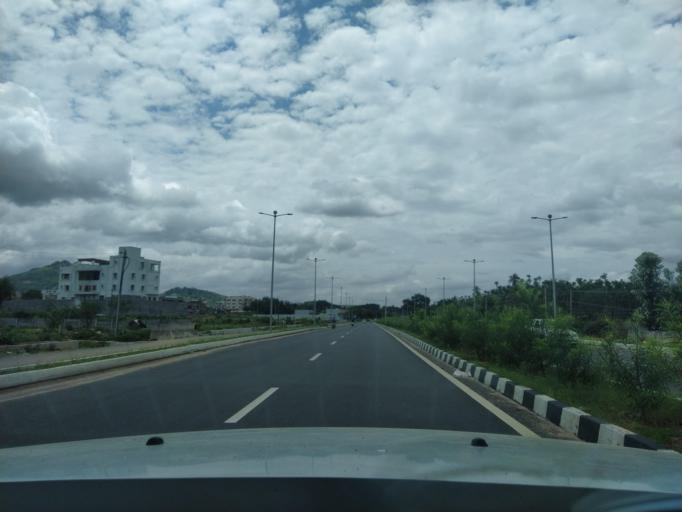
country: IN
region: Karnataka
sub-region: Tumkur
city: Tumkur
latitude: 13.3080
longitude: 77.1486
